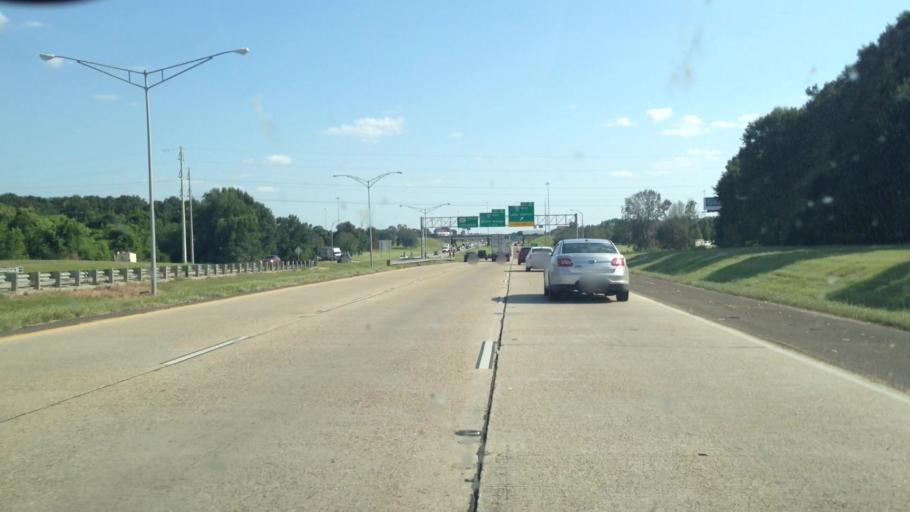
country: US
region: Louisiana
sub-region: Lafayette Parish
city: Lafayette
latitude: 30.2657
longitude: -92.0172
